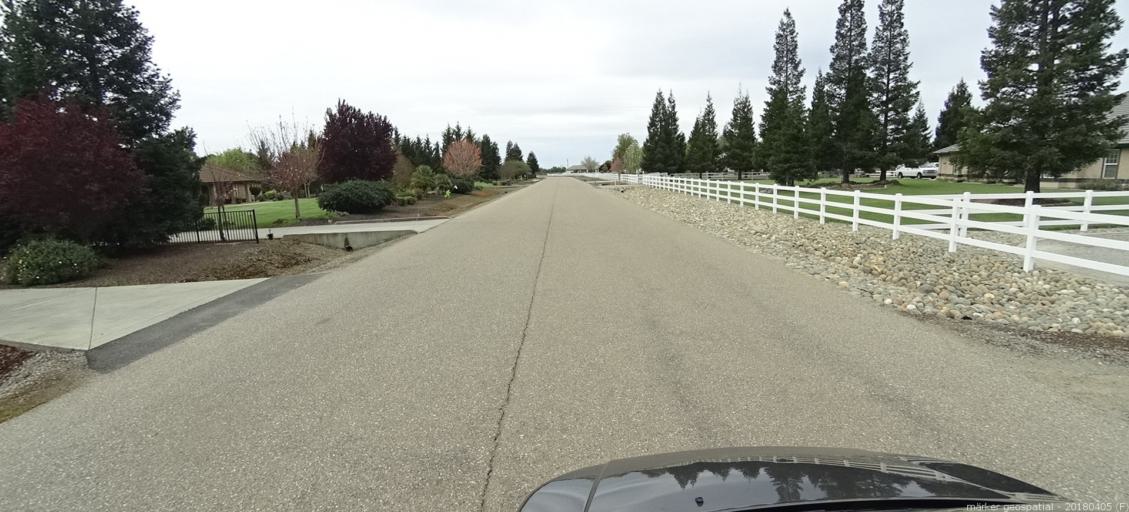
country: US
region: California
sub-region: Sacramento County
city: Galt
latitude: 38.2756
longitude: -121.3324
